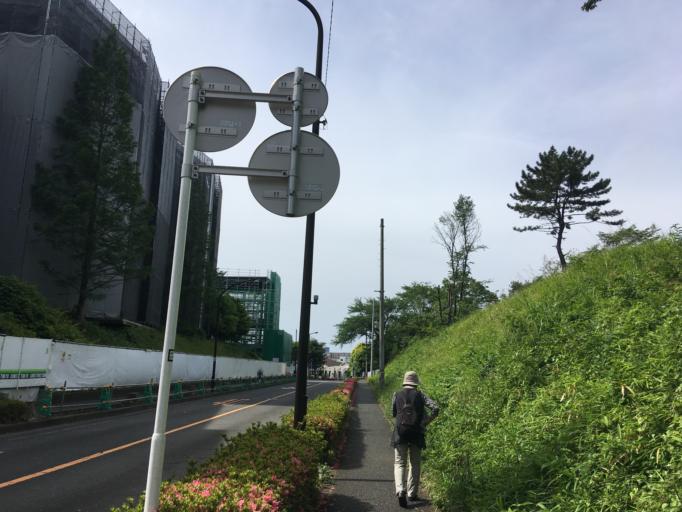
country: JP
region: Kanagawa
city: Minami-rinkan
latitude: 35.5103
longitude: 139.4696
